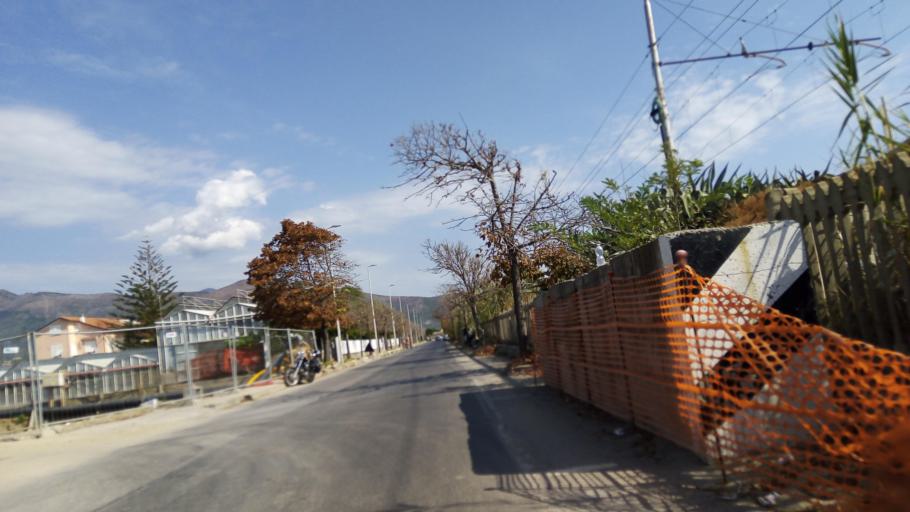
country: IT
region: Liguria
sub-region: Provincia di Savona
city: Albenga
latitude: 44.0676
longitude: 8.2251
